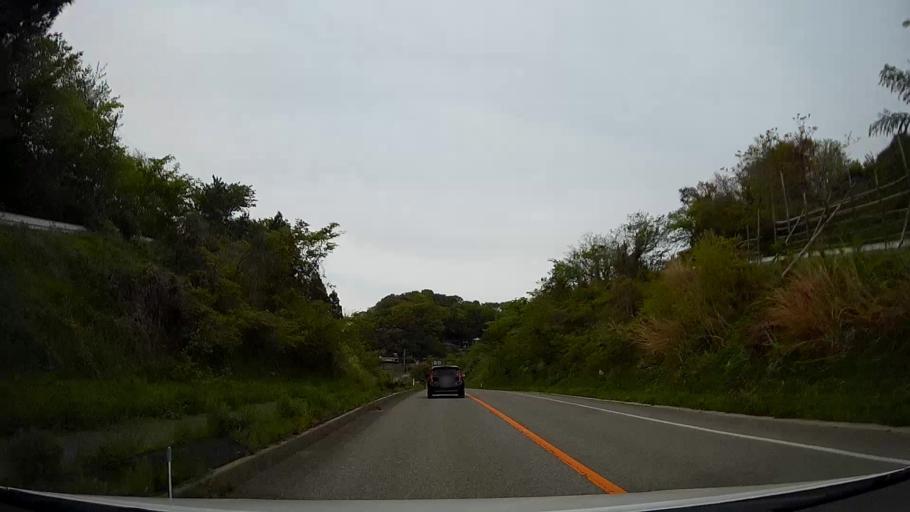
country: JP
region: Ishikawa
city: Nanao
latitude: 37.4066
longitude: 136.9594
